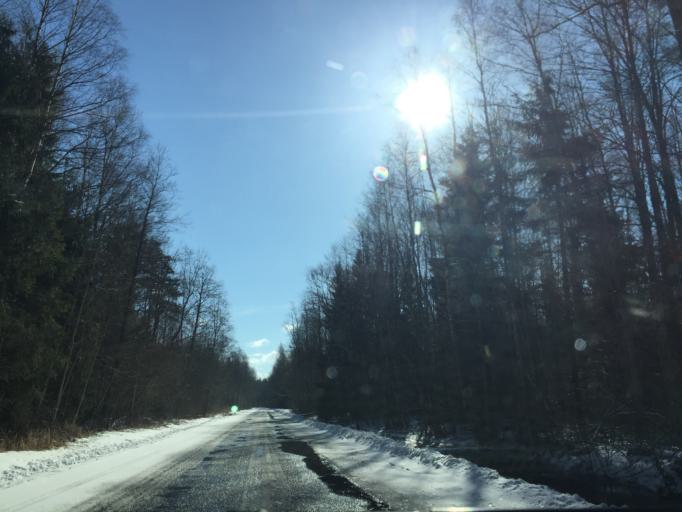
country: LV
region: Salacgrivas
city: Ainazi
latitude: 57.9993
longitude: 24.5291
